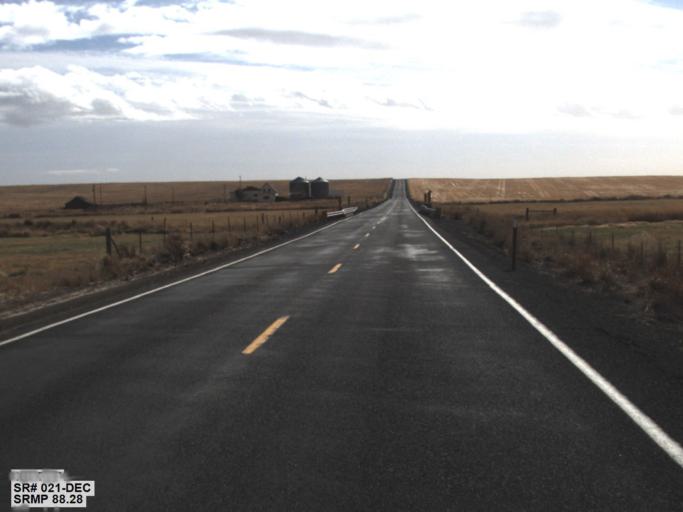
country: US
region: Washington
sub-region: Okanogan County
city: Coulee Dam
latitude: 47.7165
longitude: -118.7221
